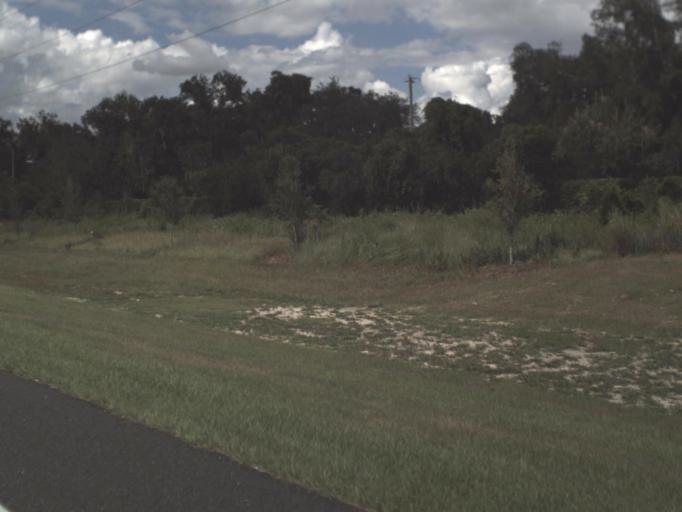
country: US
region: Florida
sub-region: Polk County
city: Highland City
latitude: 27.9429
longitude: -81.8631
